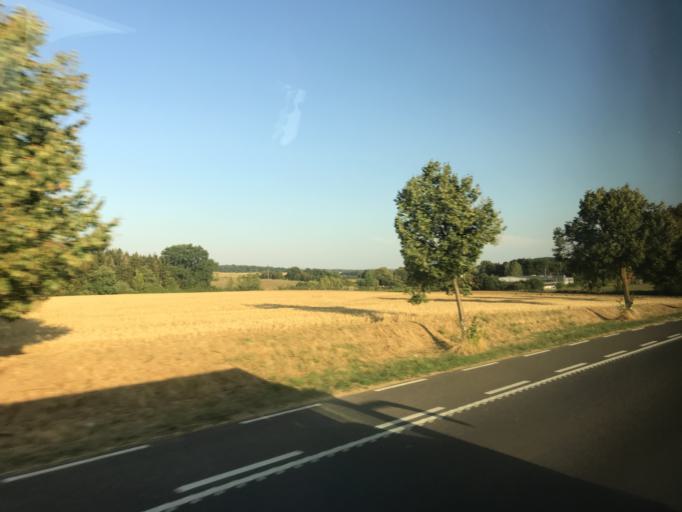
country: LU
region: Luxembourg
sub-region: Canton de Luxembourg
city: Weiler-la-Tour
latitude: 49.5369
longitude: 6.1779
